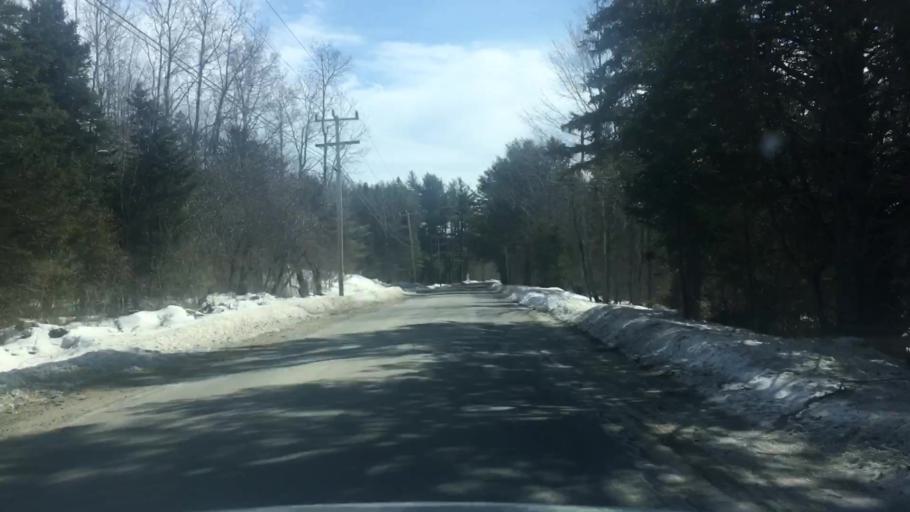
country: US
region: Maine
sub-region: Penobscot County
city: Holden
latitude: 44.7543
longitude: -68.6353
